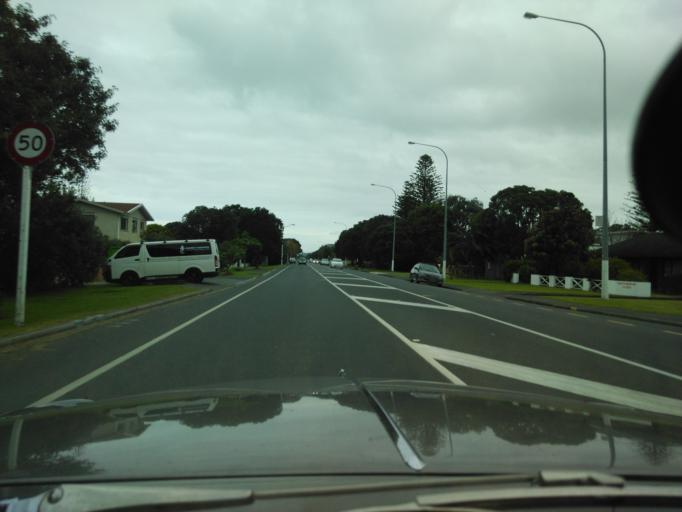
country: NZ
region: Auckland
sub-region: Auckland
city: Rothesay Bay
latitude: -36.5754
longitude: 174.6906
